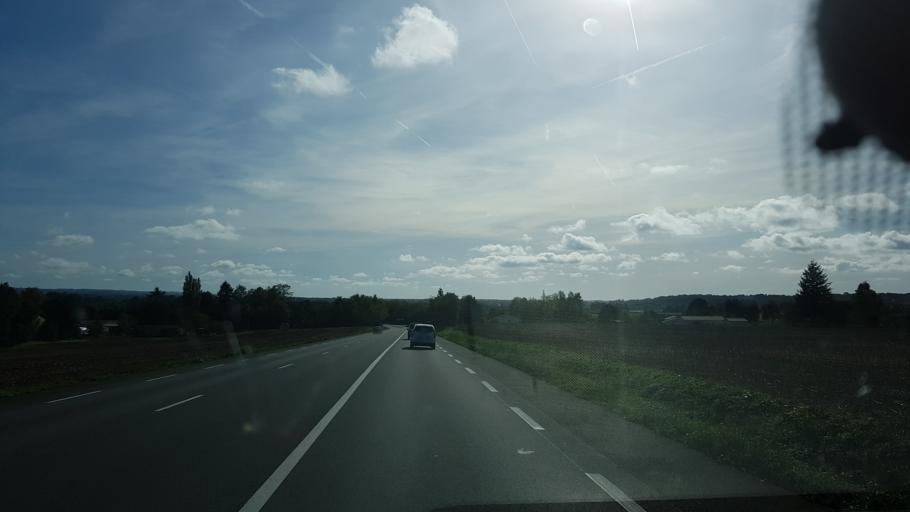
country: FR
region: Poitou-Charentes
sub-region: Departement de la Charente
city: Chasseneuil-sur-Bonnieure
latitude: 45.8478
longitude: 0.4617
